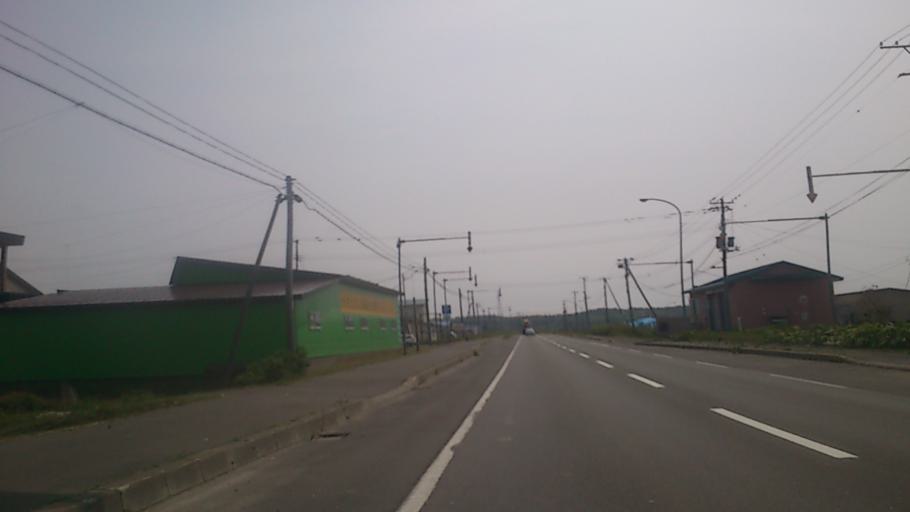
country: JP
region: Hokkaido
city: Nemuro
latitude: 43.2719
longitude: 145.4971
